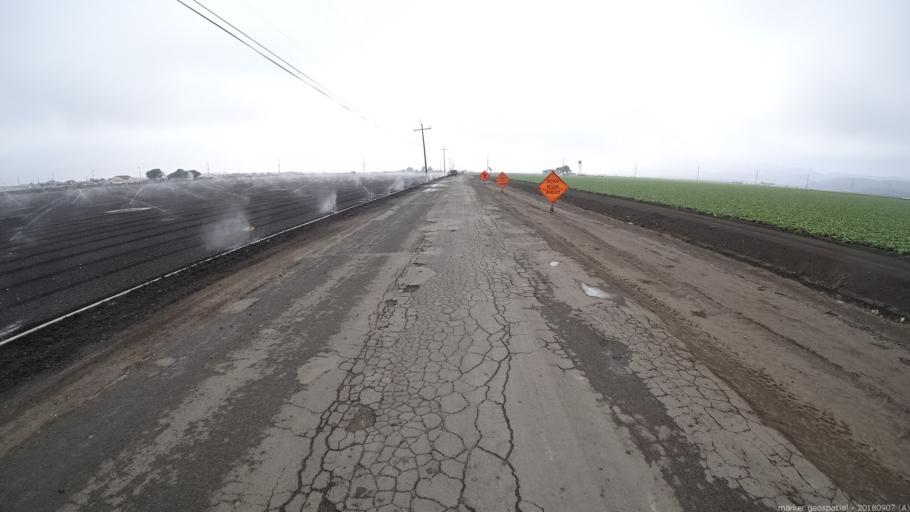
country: US
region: California
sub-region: Monterey County
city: Salinas
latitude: 36.6603
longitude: -121.6951
